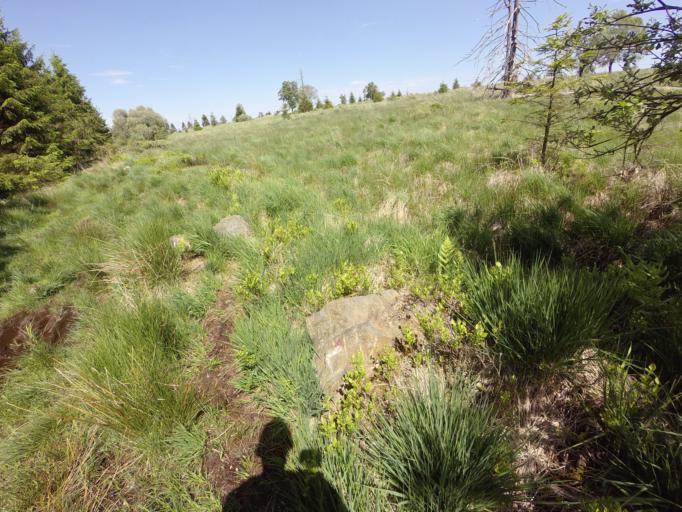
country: BE
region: Wallonia
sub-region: Province de Liege
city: Jalhay
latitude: 50.5152
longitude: 6.0357
